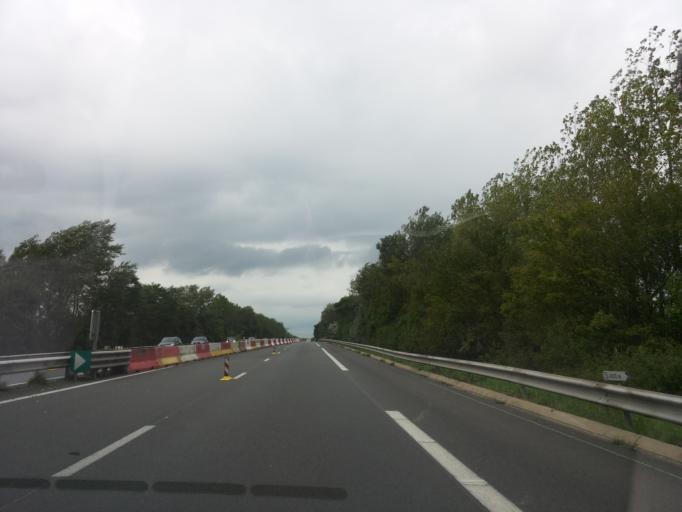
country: FR
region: Nord-Pas-de-Calais
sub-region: Departement du Pas-de-Calais
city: Les Attaques
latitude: 50.9105
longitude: 1.9432
